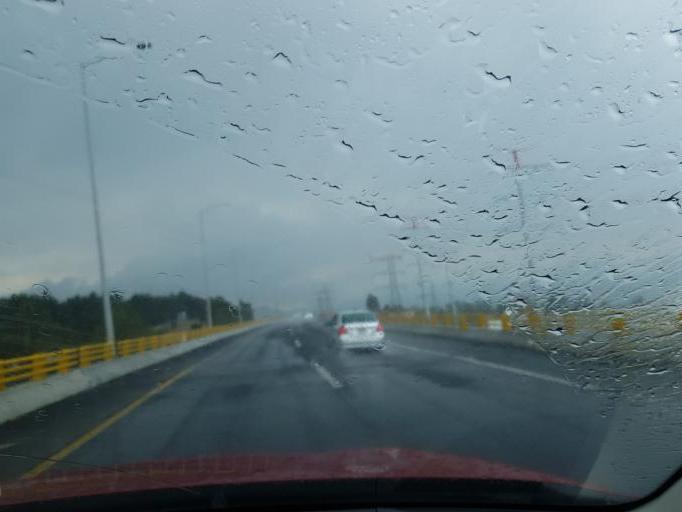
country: MX
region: Mexico
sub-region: Ocoyoacac
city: San Antonio el Llanito
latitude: 19.2822
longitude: -99.4875
